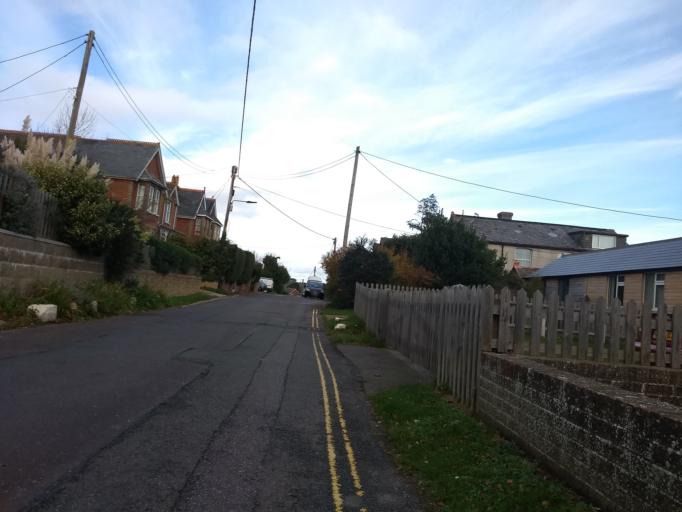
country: GB
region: England
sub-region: Isle of Wight
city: Freshwater
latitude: 50.6748
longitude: -1.5169
